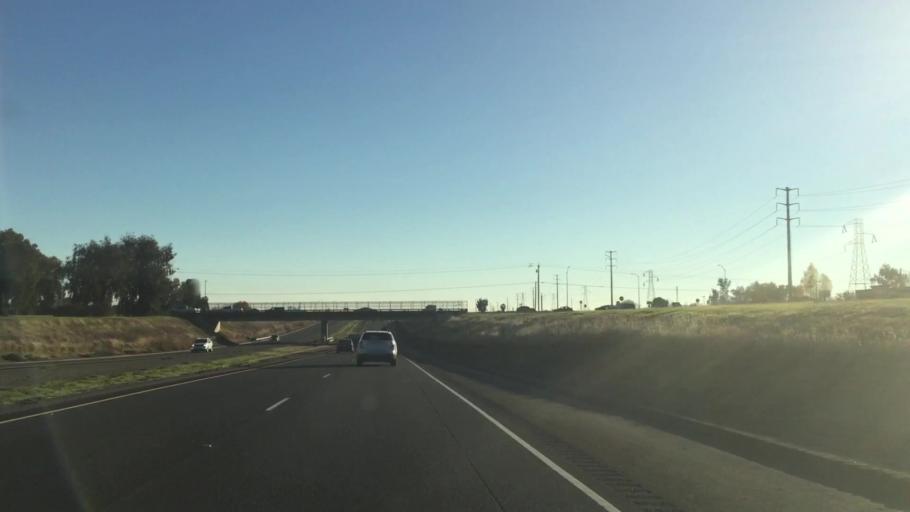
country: US
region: California
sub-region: Yuba County
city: Olivehurst
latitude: 39.0790
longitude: -121.5417
